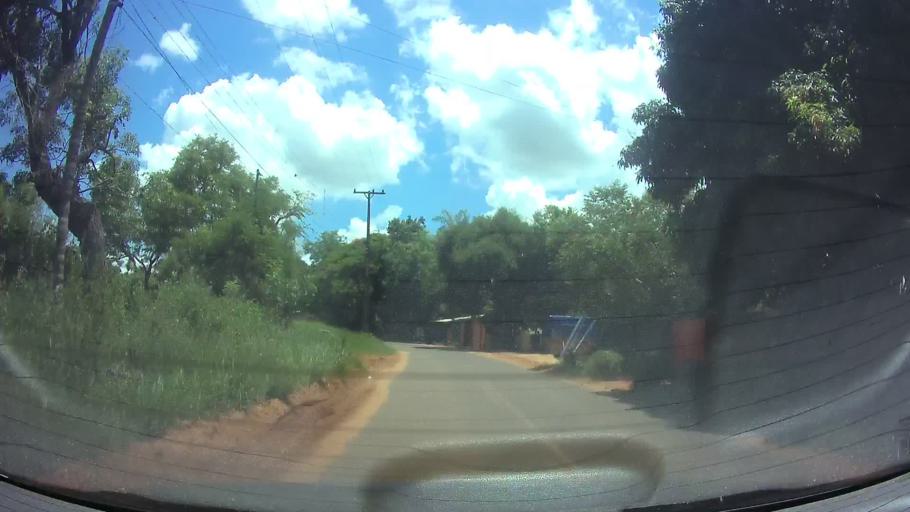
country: PY
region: Central
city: Itaugua
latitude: -25.3745
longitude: -57.3660
